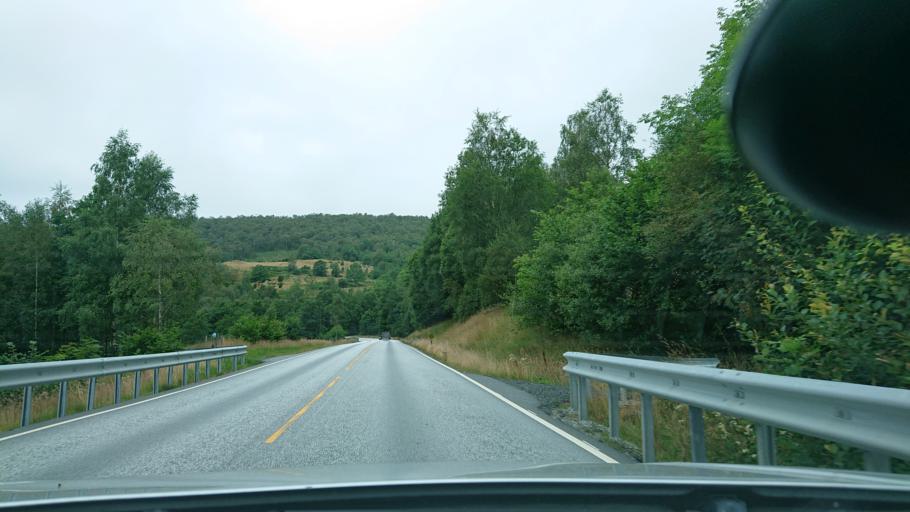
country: NO
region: Rogaland
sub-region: Hjelmeland
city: Hjelmelandsvagen
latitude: 59.1717
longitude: 6.1642
